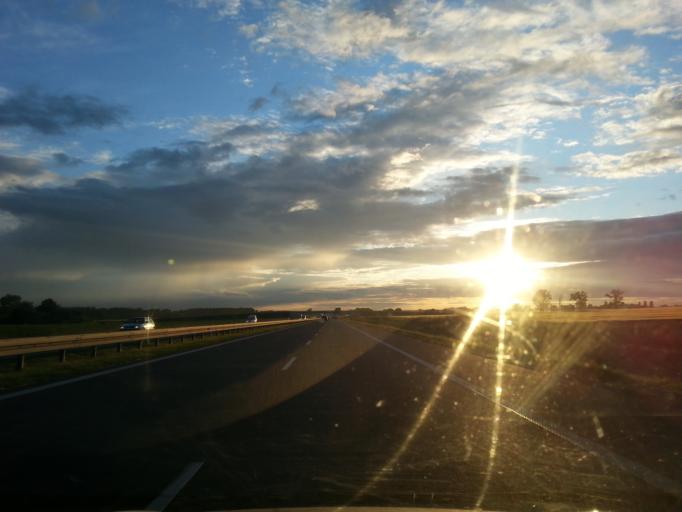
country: PL
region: Lower Silesian Voivodeship
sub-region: Powiat olesnicki
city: Sycow
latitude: 51.3015
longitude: 17.6416
